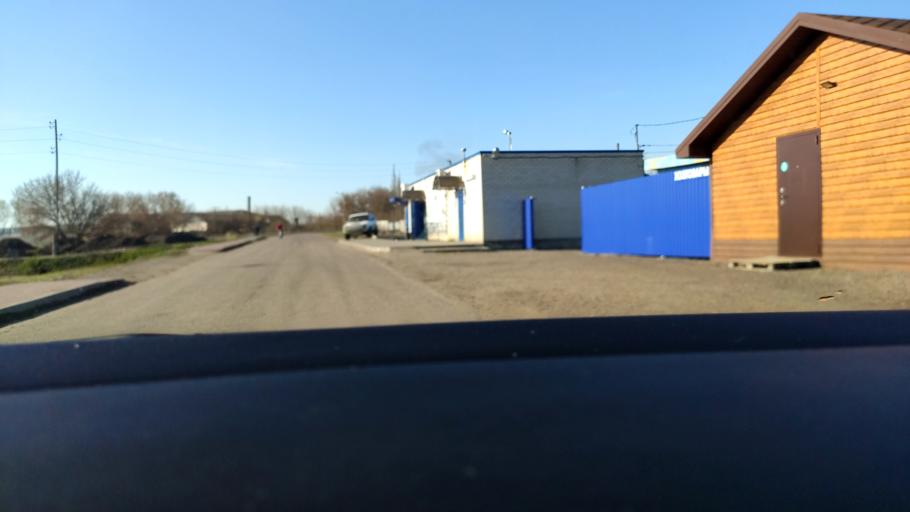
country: RU
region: Voronezj
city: Maslovka
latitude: 51.5022
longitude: 39.2942
